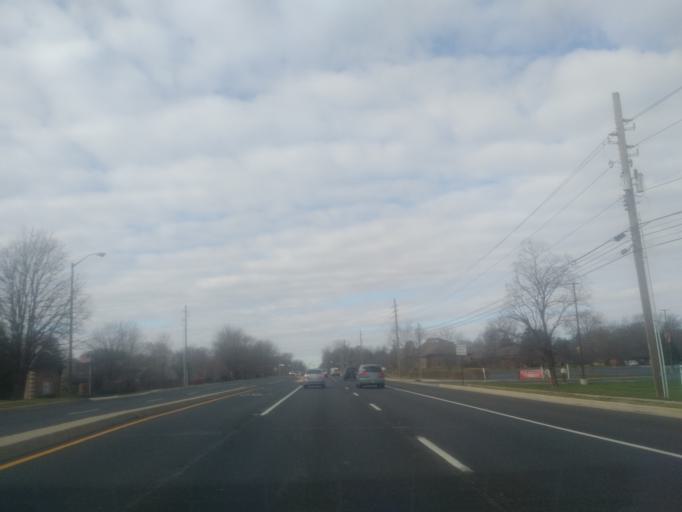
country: US
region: Indiana
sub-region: Marion County
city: Meridian Hills
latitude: 39.9125
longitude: -86.1611
